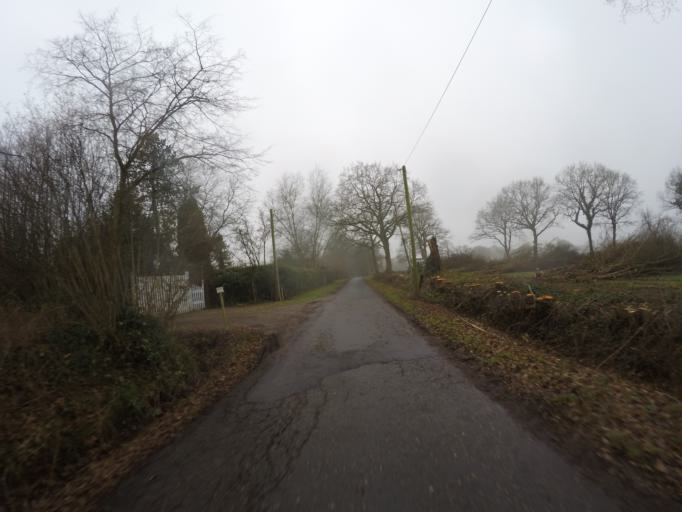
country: DE
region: Schleswig-Holstein
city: Quickborn
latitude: 53.7174
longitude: 9.9010
